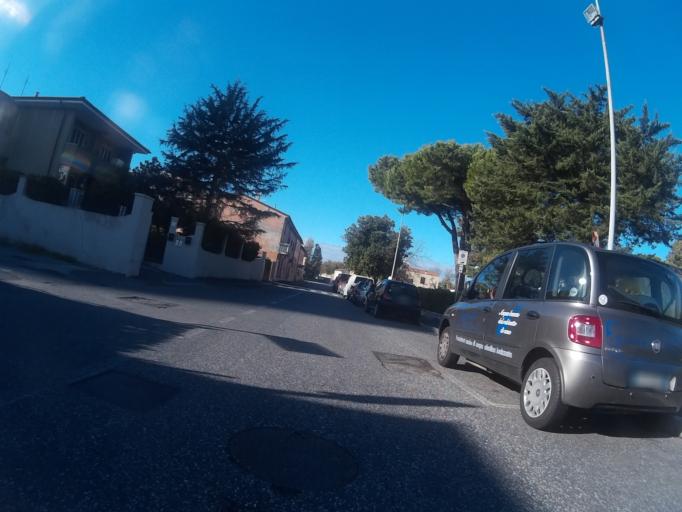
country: IT
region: Tuscany
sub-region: Provincia di Livorno
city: Livorno
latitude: 43.5623
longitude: 10.3414
